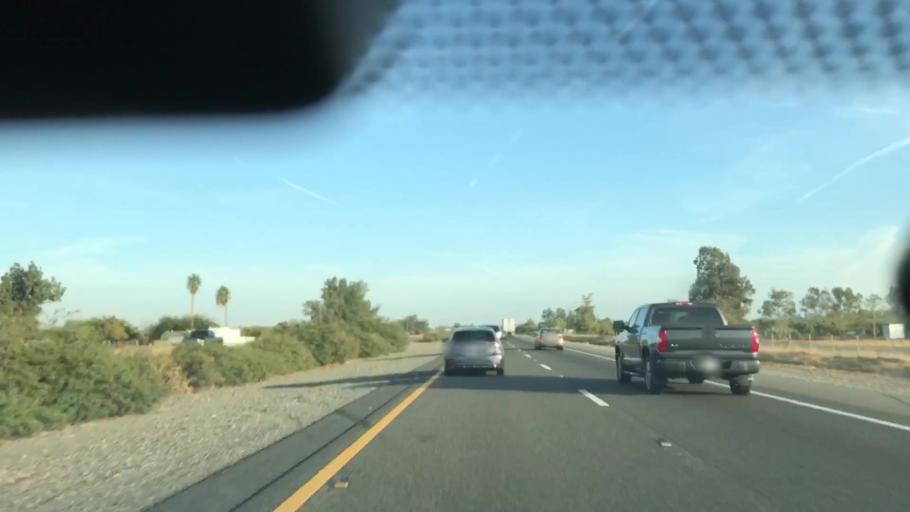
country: US
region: California
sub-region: Glenn County
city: Orland
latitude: 39.7010
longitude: -122.2055
